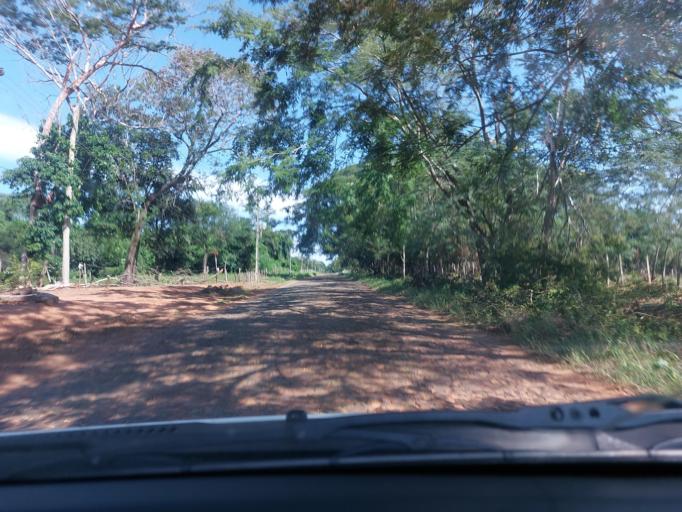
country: PY
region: San Pedro
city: Itacurubi del Rosario
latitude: -24.5719
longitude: -56.5972
